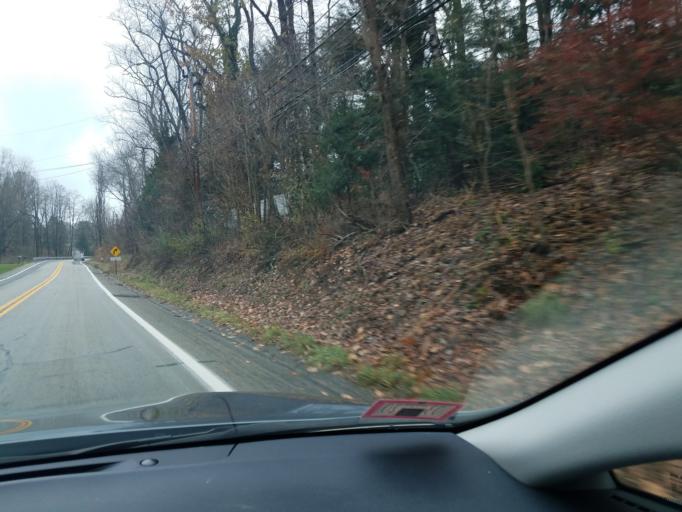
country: US
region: Pennsylvania
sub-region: Allegheny County
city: Franklin Park
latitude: 40.5677
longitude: -80.0695
